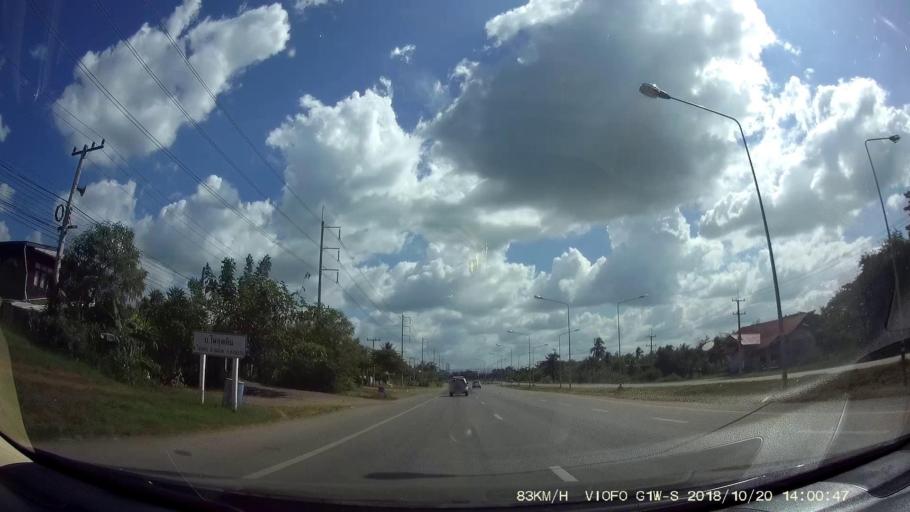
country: TH
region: Khon Kaen
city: Chum Phae
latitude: 16.5098
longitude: 102.1187
